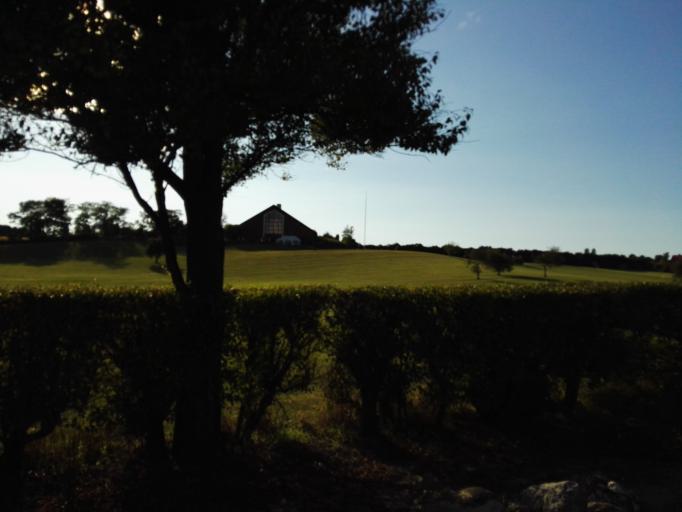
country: DK
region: Zealand
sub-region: Odsherred Kommune
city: Nykobing Sjaelland
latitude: 55.9032
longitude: 11.6682
